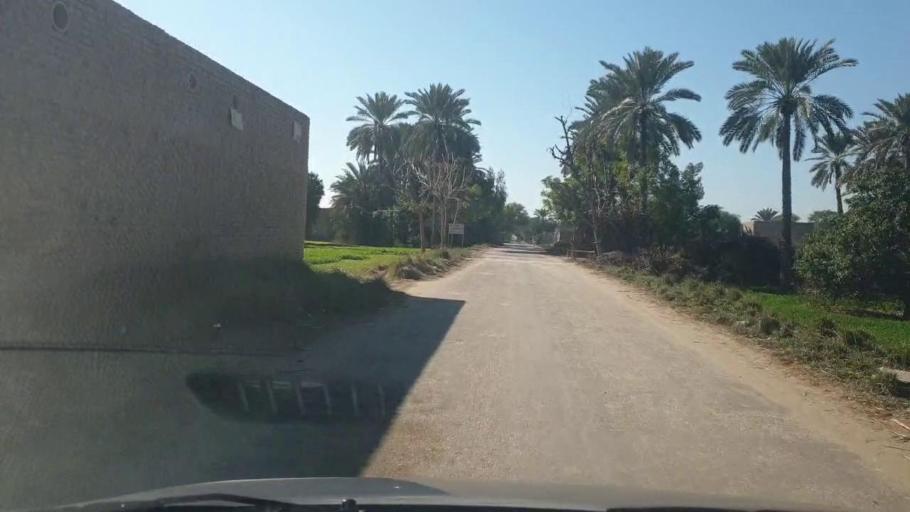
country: PK
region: Sindh
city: Bozdar
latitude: 27.1492
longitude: 68.6511
